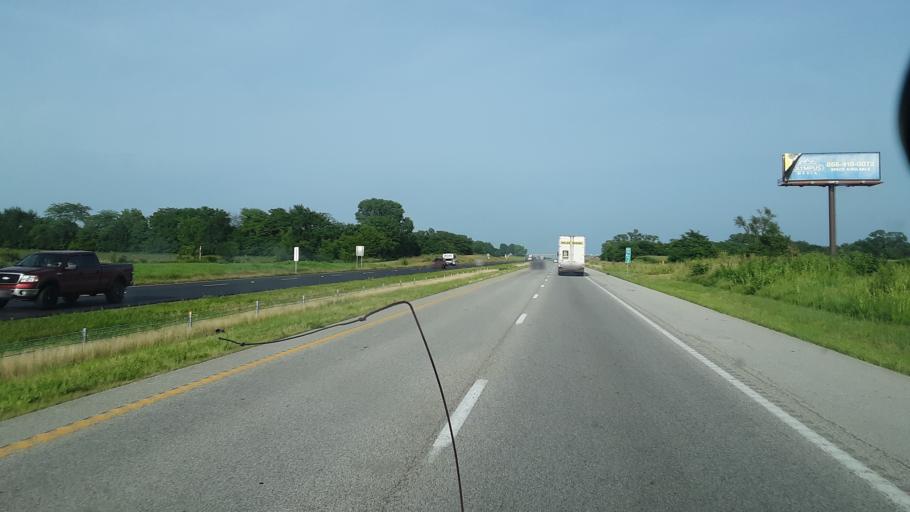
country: US
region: Missouri
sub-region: Saline County
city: Sweet Springs
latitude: 38.9736
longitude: -93.3437
